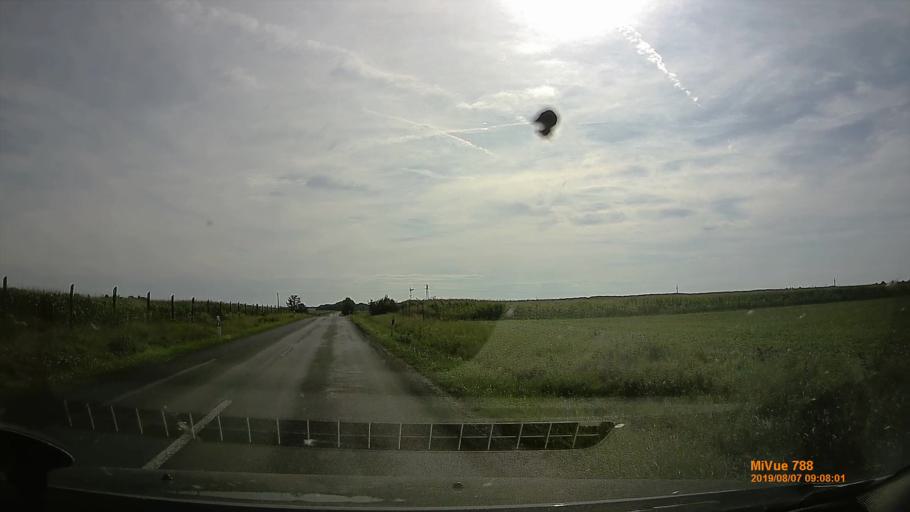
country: HU
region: Zala
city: Pacsa
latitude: 46.7272
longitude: 17.0451
